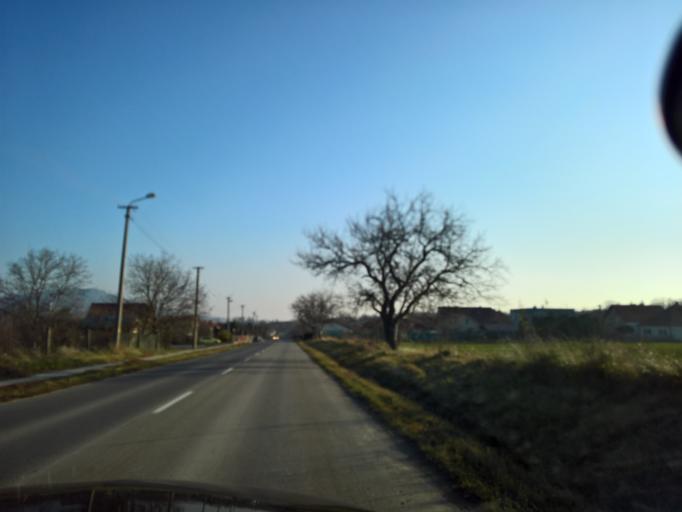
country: SK
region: Nitriansky
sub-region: Okres Nitra
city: Nitra
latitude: 48.3158
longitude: 18.0323
